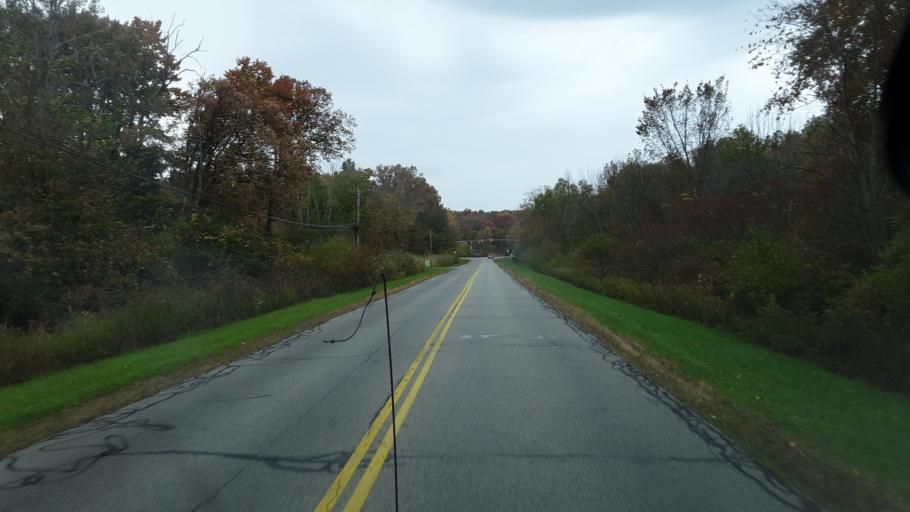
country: US
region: Ohio
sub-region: Portage County
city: Kent
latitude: 41.1319
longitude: -81.3465
